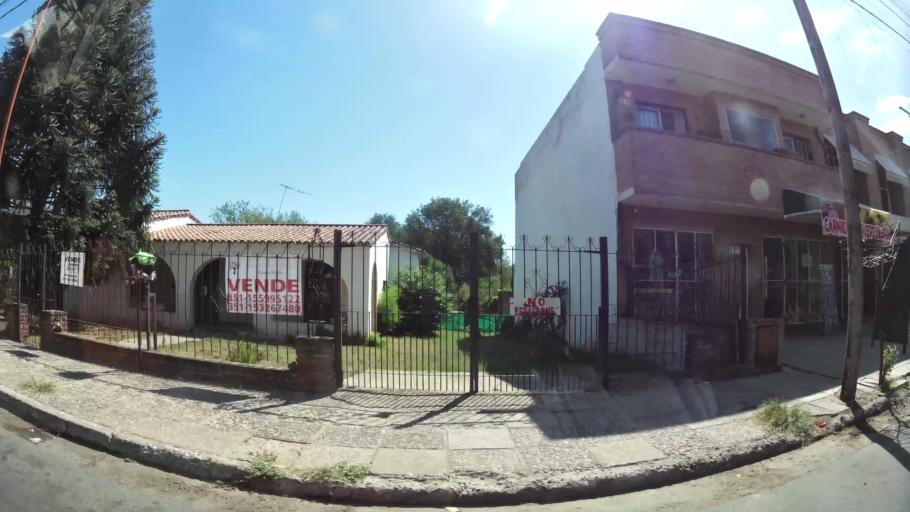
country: AR
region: Cordoba
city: Villa Allende
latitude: -31.2967
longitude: -64.3007
